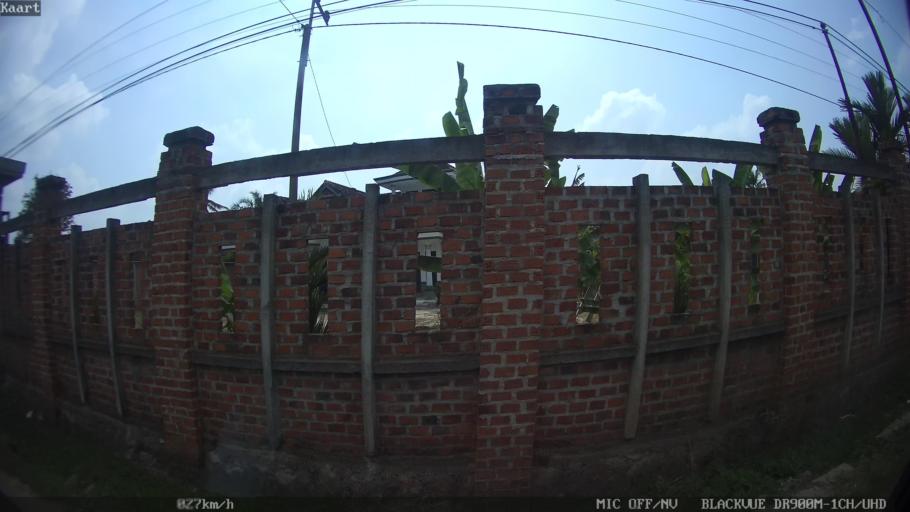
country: ID
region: Lampung
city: Pringsewu
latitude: -5.3769
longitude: 104.9663
